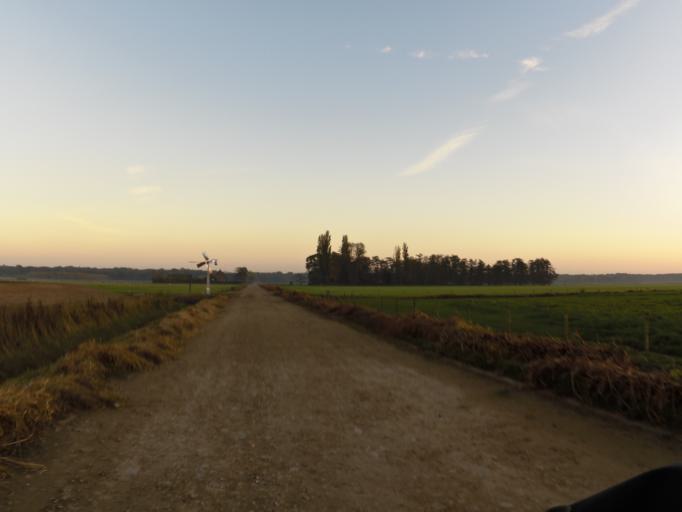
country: NL
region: North Brabant
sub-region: Gemeente Vught
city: Vught
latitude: 51.6777
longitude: 5.2740
